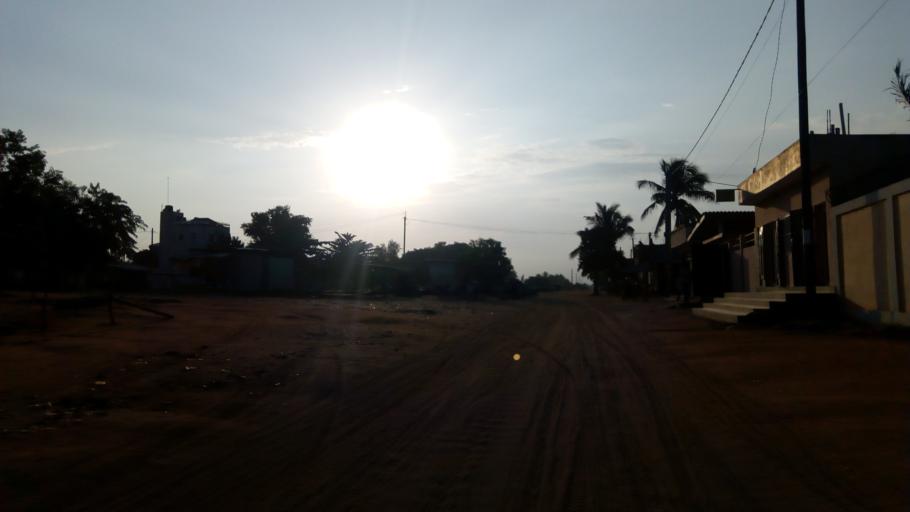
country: TG
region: Maritime
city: Lome
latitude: 6.1840
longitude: 1.1811
